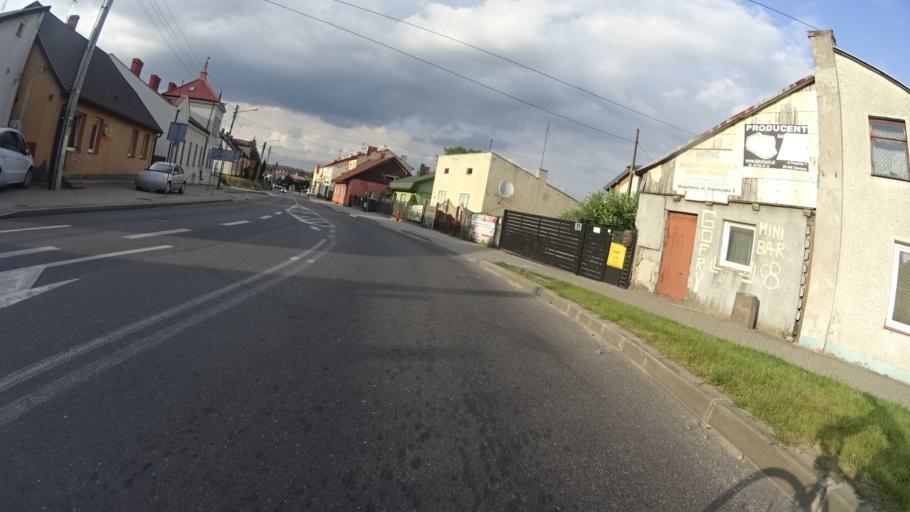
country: PL
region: Masovian Voivodeship
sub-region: Powiat grojecki
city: Mogielnica
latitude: 51.6913
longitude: 20.7213
